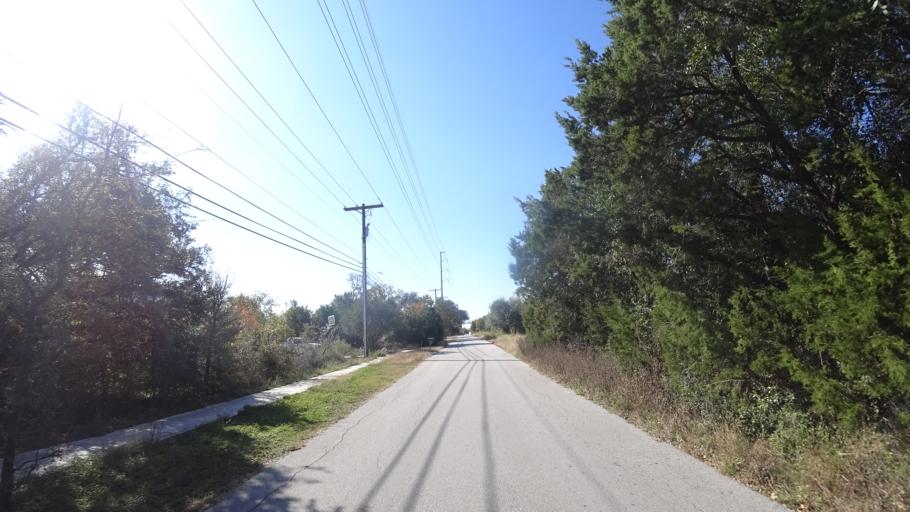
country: US
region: Texas
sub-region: Travis County
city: Barton Creek
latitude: 30.2313
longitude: -97.8584
